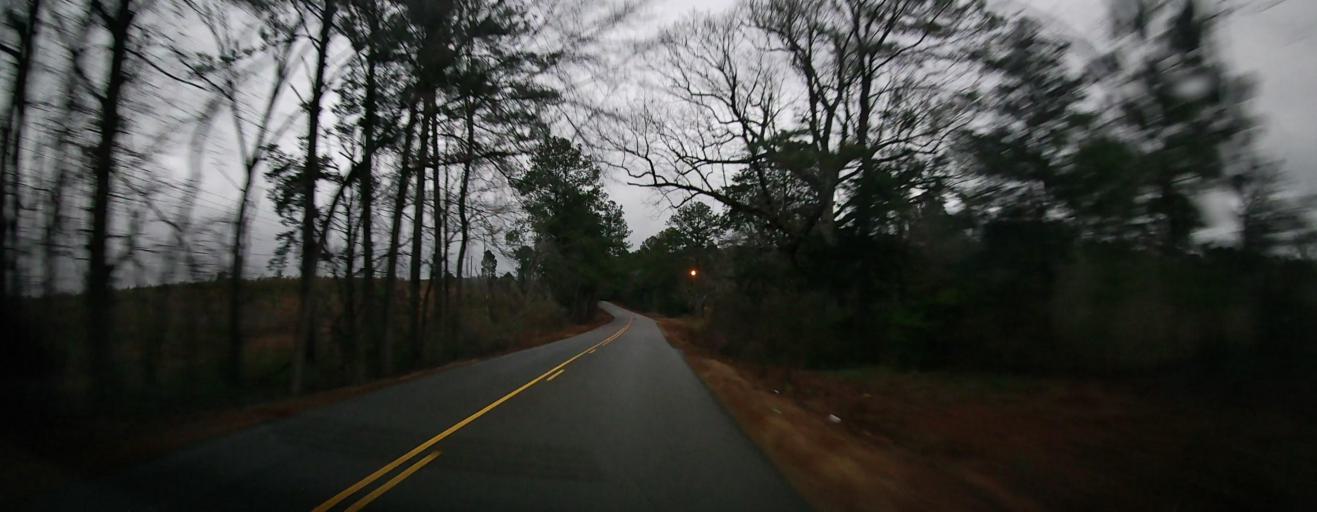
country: US
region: Alabama
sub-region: Tuscaloosa County
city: Vance
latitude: 33.1327
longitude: -87.2298
